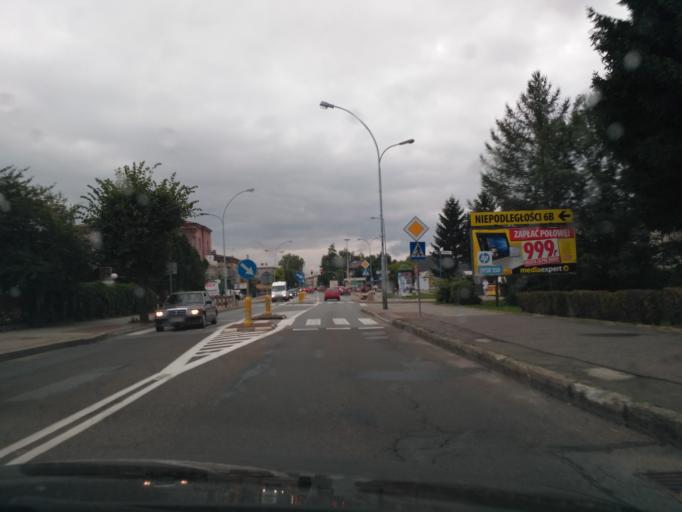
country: PL
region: Subcarpathian Voivodeship
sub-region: Krosno
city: Krosno
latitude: 49.6854
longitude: 21.7711
